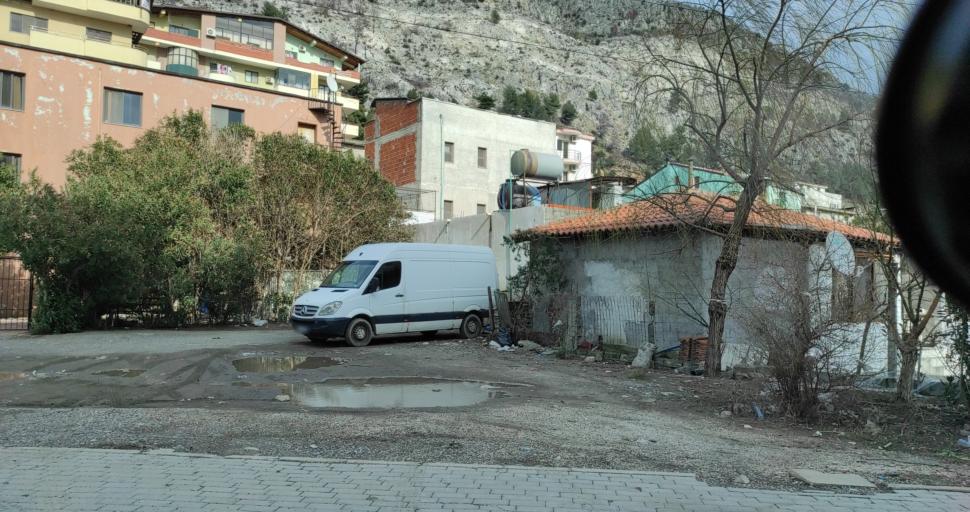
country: AL
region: Lezhe
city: Shengjin
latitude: 41.8143
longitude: 19.5908
